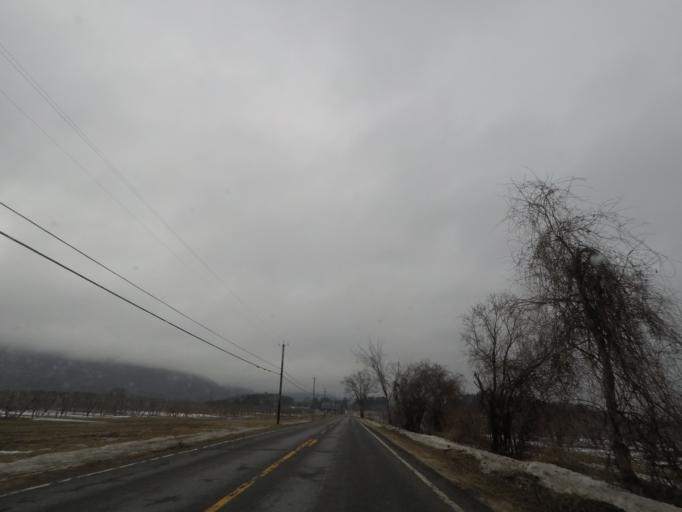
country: US
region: New York
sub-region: Albany County
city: Voorheesville
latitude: 42.6544
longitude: -73.9668
